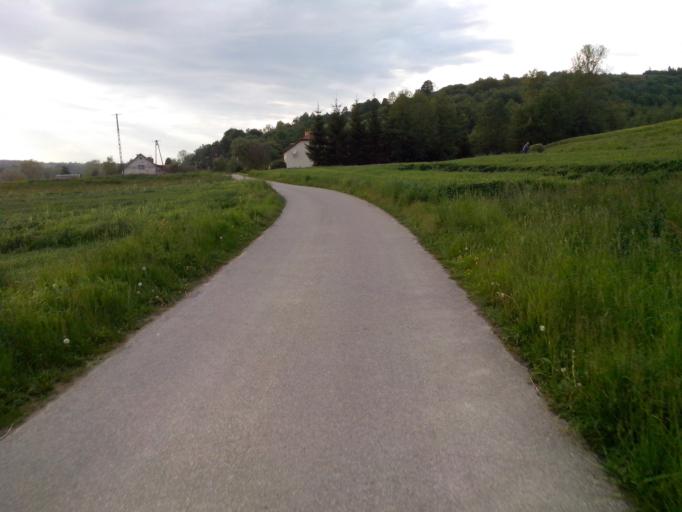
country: PL
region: Subcarpathian Voivodeship
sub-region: Powiat strzyzowski
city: Jawornik
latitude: 49.8199
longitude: 21.8438
